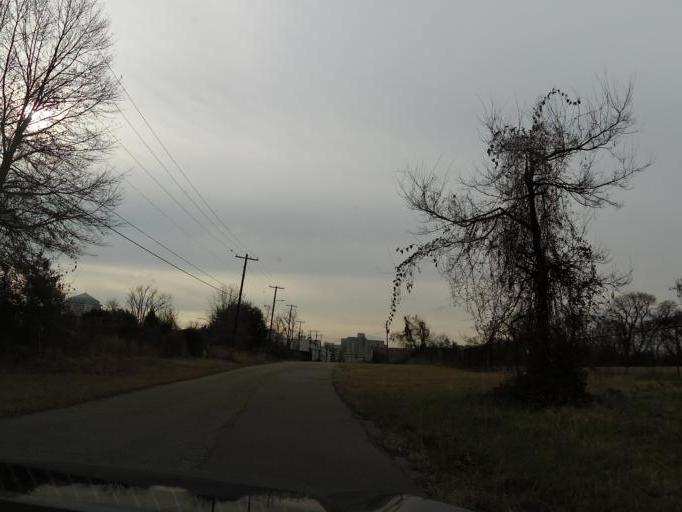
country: US
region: Alabama
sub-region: Montgomery County
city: Montgomery
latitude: 32.3881
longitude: -86.3122
